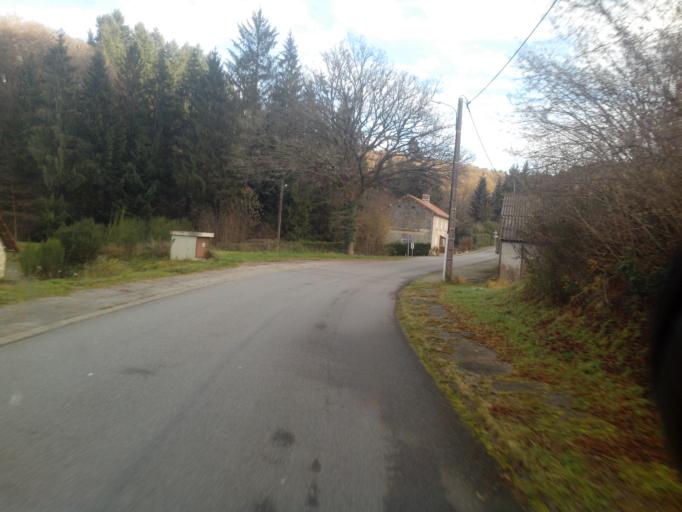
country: FR
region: Limousin
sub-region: Departement de la Haute-Vienne
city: Eymoutiers
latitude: 45.6846
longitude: 1.7936
